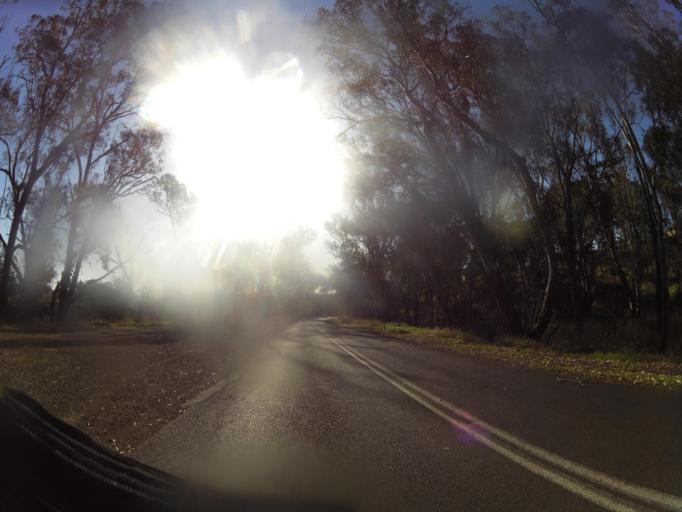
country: AU
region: Victoria
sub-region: Murrindindi
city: Kinglake West
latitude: -37.0202
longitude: 145.1128
